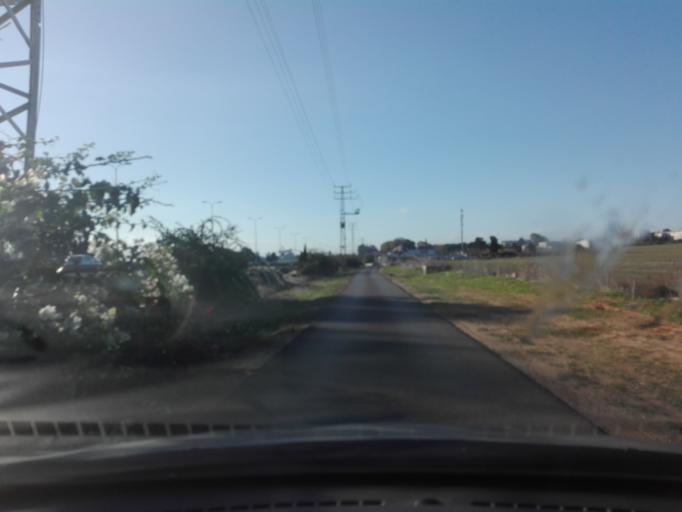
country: IL
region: Central District
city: Netanya
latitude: 32.3076
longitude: 34.8645
